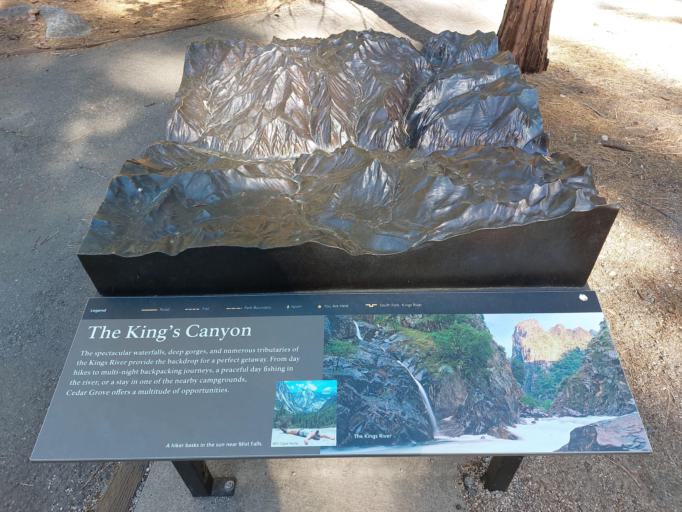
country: US
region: California
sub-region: Tulare County
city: Three Rivers
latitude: 36.7907
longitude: -118.6710
